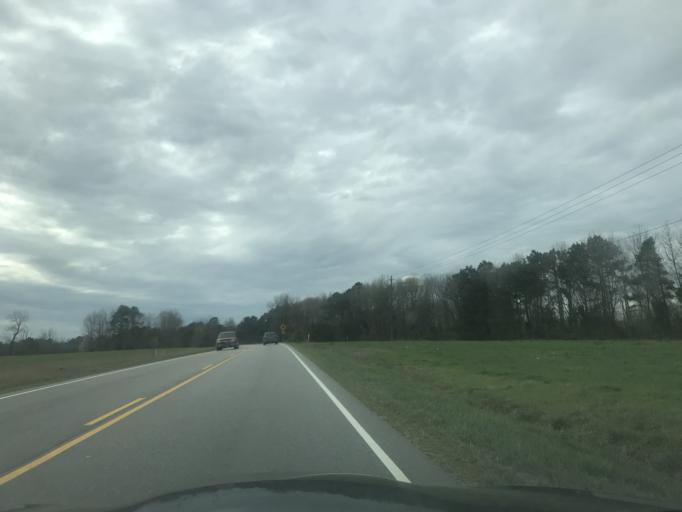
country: US
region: North Carolina
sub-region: Franklin County
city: Franklinton
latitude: 36.0937
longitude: -78.4067
